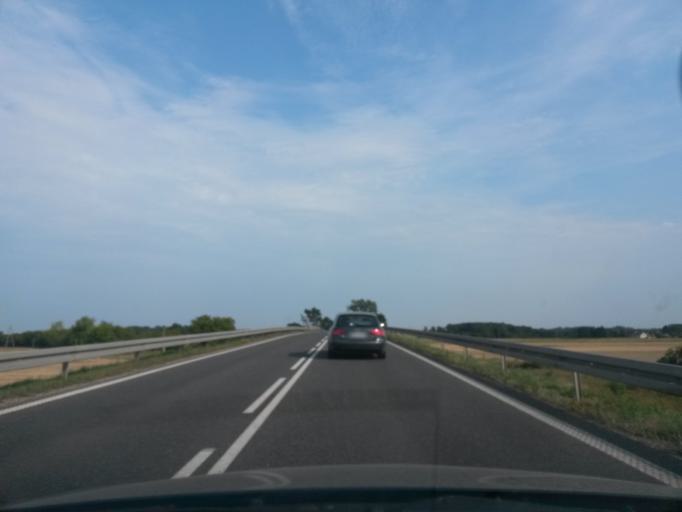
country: PL
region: Masovian Voivodeship
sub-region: Powiat sierpecki
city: Sierpc
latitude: 52.8370
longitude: 19.7371
